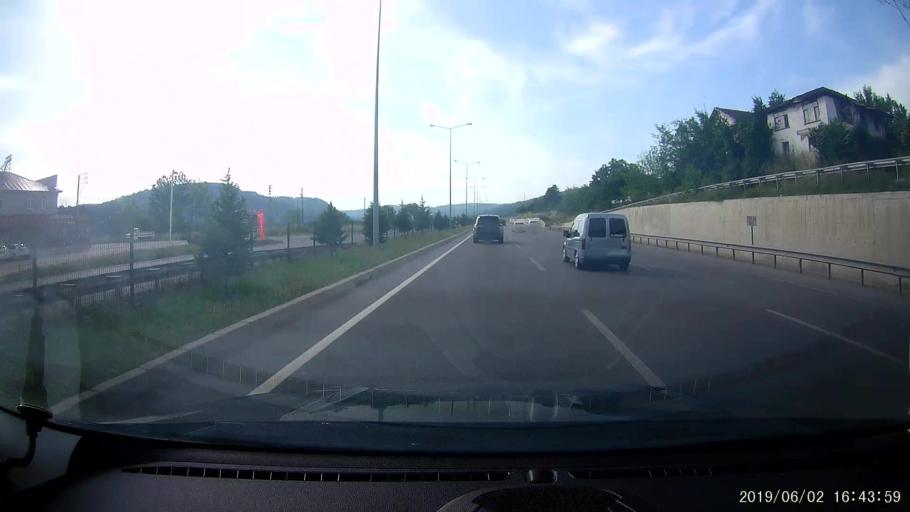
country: TR
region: Samsun
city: Kavak
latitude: 41.1436
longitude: 36.1174
